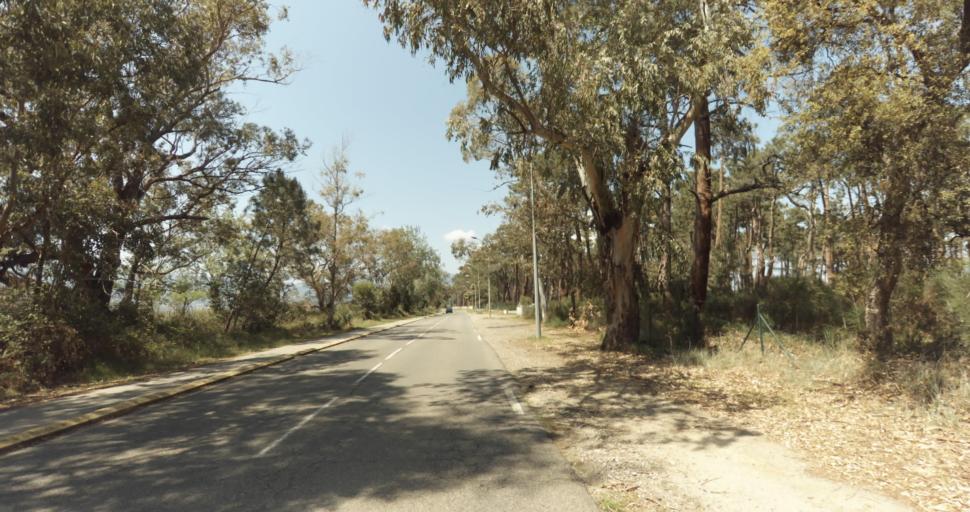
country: FR
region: Corsica
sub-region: Departement de la Haute-Corse
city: Biguglia
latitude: 42.6178
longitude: 9.4768
